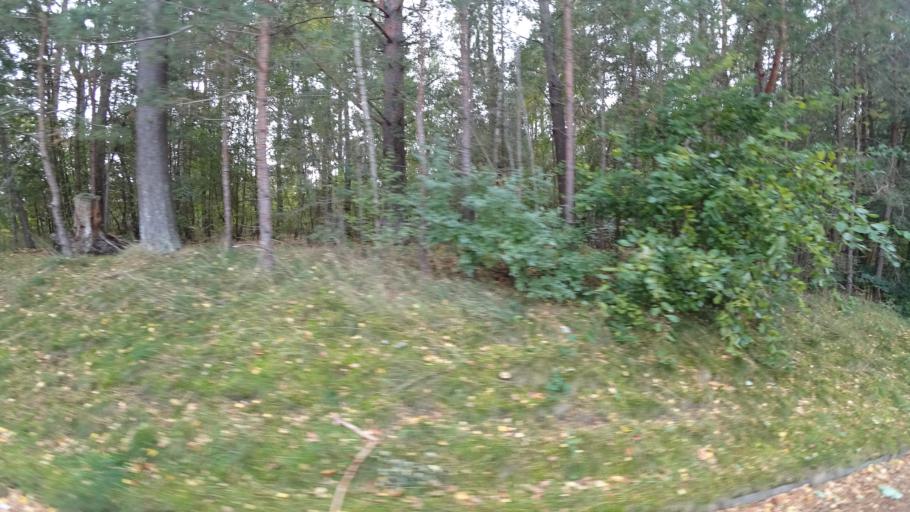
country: SE
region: Skane
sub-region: Kavlinge Kommun
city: Hofterup
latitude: 55.8077
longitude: 12.9792
